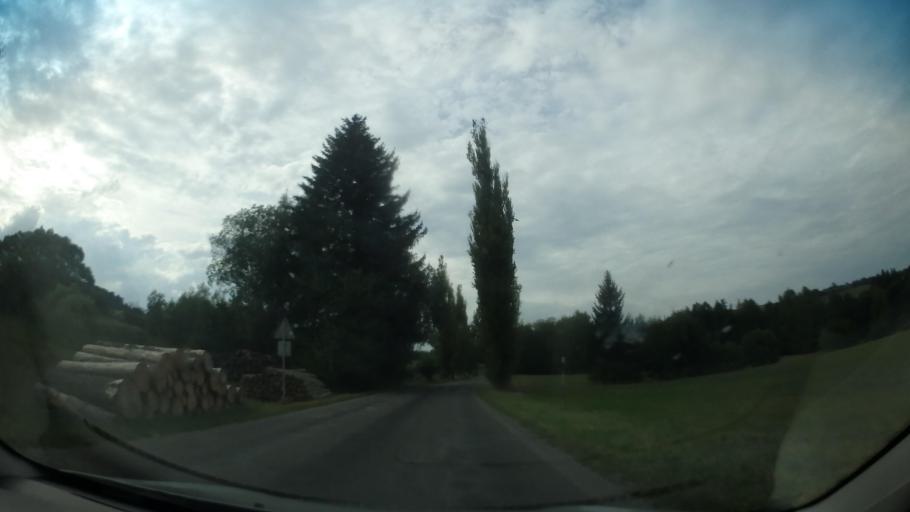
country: CZ
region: Pardubicky
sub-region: Okres Chrudim
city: Sec
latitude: 49.8385
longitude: 15.6973
